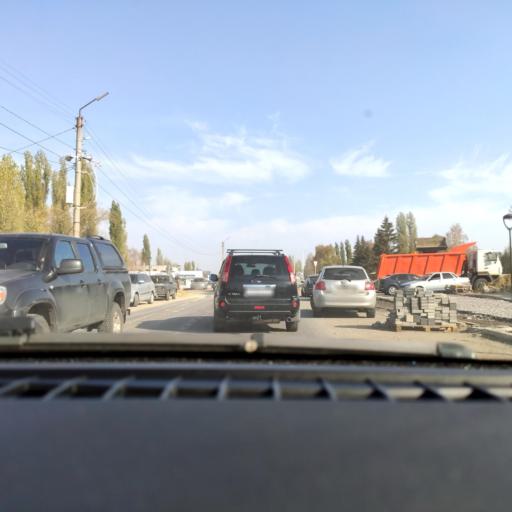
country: RU
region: Voronezj
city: Novaya Usman'
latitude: 51.6460
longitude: 39.4158
